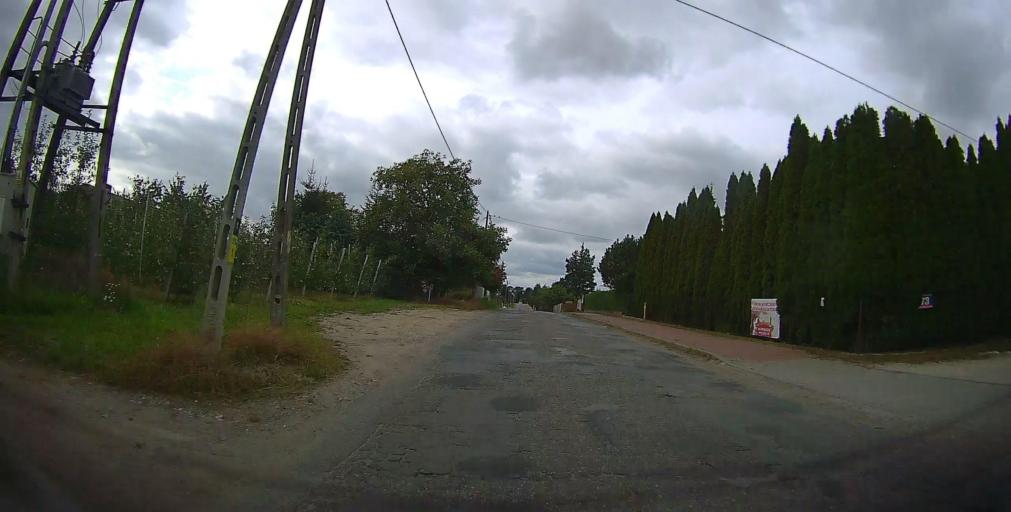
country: PL
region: Masovian Voivodeship
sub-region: Powiat grojecki
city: Belsk Duzy
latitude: 51.8174
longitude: 20.8250
